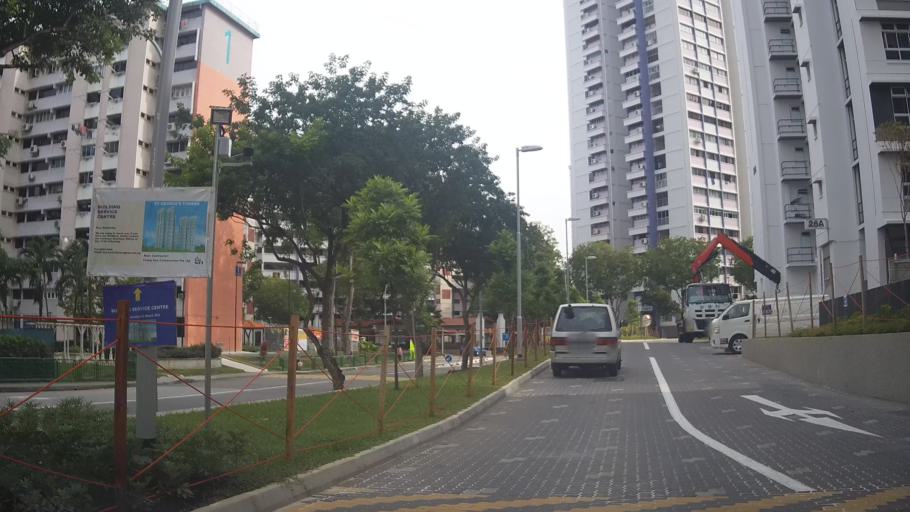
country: SG
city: Singapore
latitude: 1.3227
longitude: 103.8618
